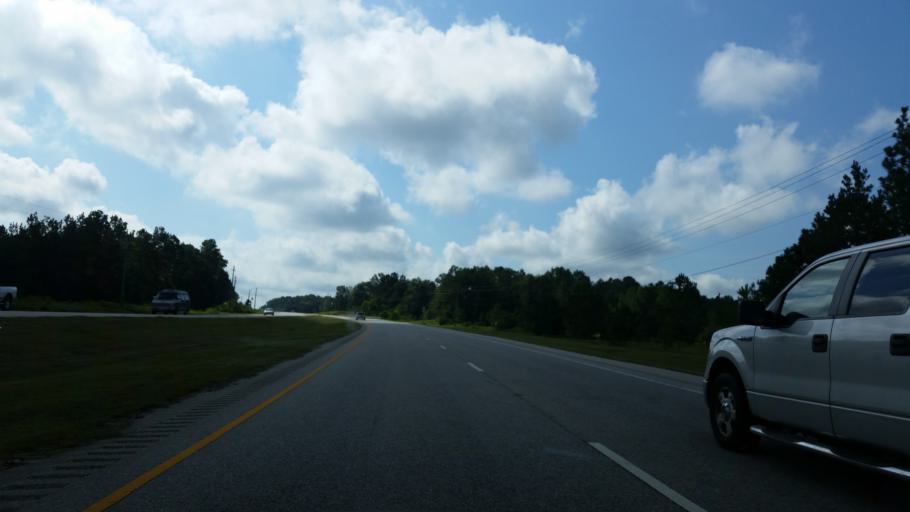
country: US
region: Alabama
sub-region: Baldwin County
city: Bay Minette
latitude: 30.8991
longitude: -87.7944
